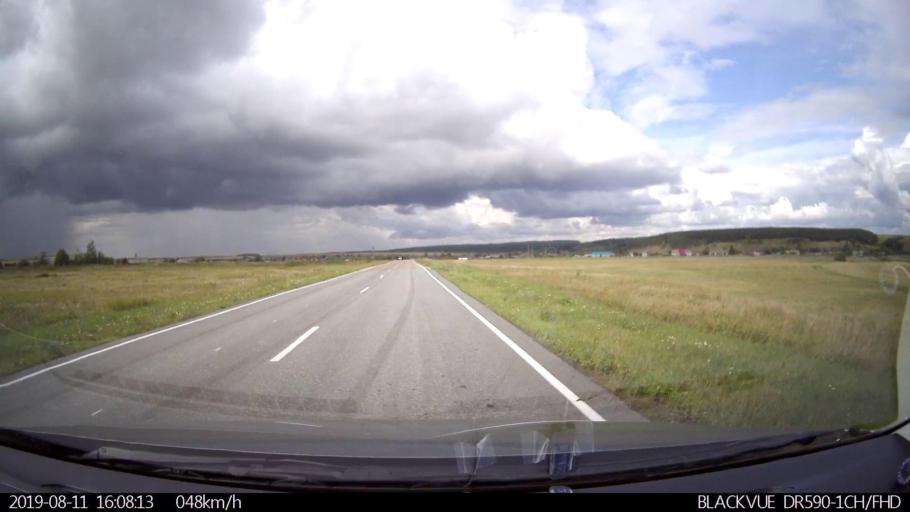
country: RU
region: Ulyanovsk
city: Ignatovka
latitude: 53.9829
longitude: 47.6477
